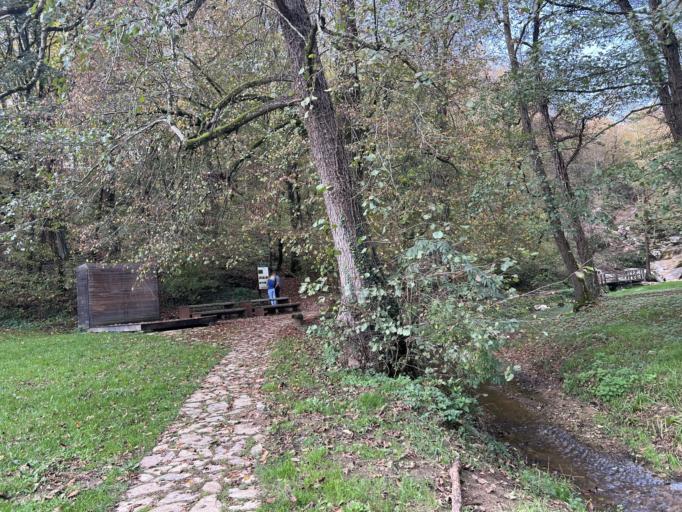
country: SI
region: Skocjan
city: Skocjan
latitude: 45.9060
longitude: 15.2338
